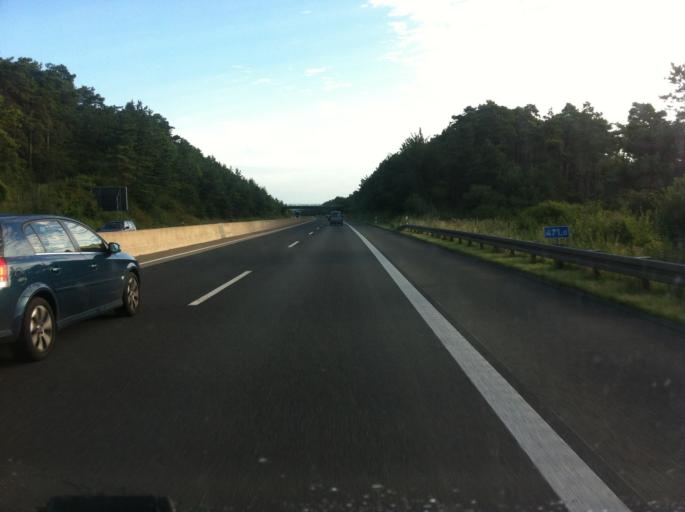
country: DE
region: North Rhine-Westphalia
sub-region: Regierungsbezirk Koln
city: Mechernich
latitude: 50.5390
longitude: 6.6762
